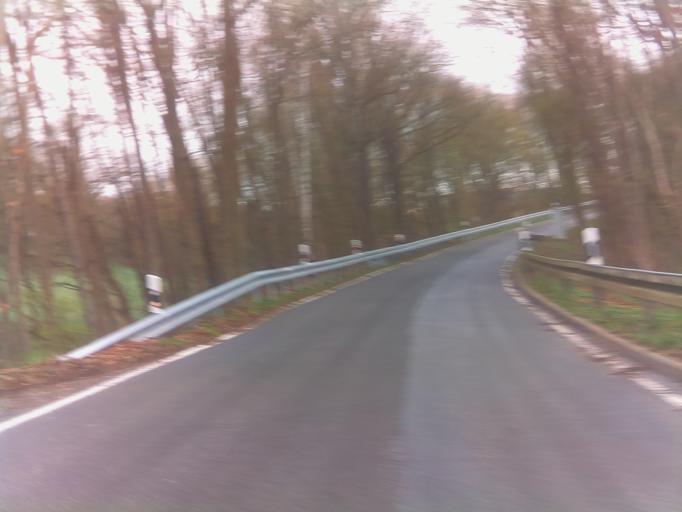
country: DE
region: Rheinland-Pfalz
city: Burgsponheim
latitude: 49.8305
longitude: 7.7126
